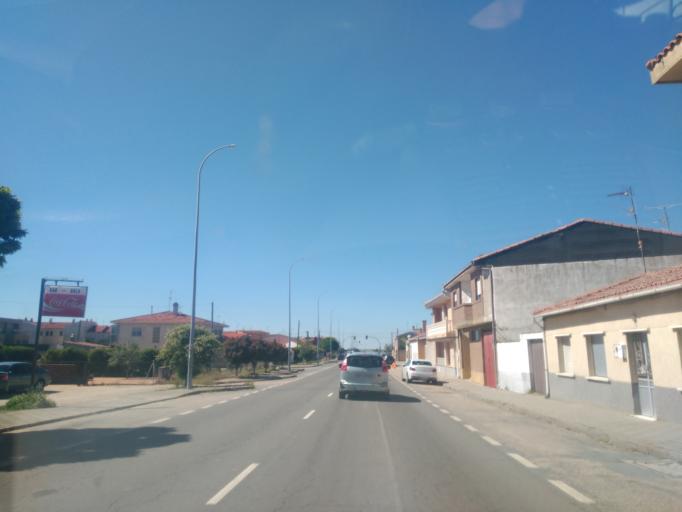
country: ES
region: Castille and Leon
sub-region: Provincia de Salamanca
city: Calvarrasa de Arriba
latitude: 40.9061
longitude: -5.5933
